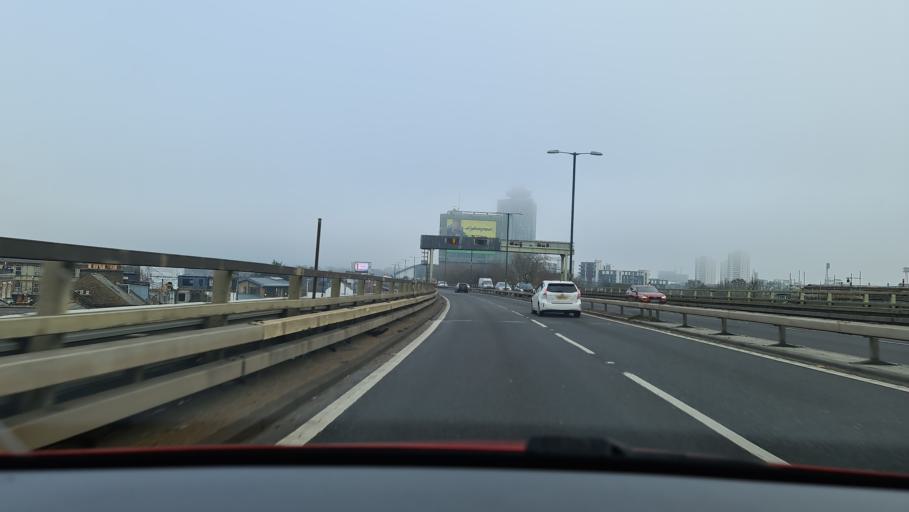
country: GB
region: England
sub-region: Greater London
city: Brentford
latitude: 51.4890
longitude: -0.3130
